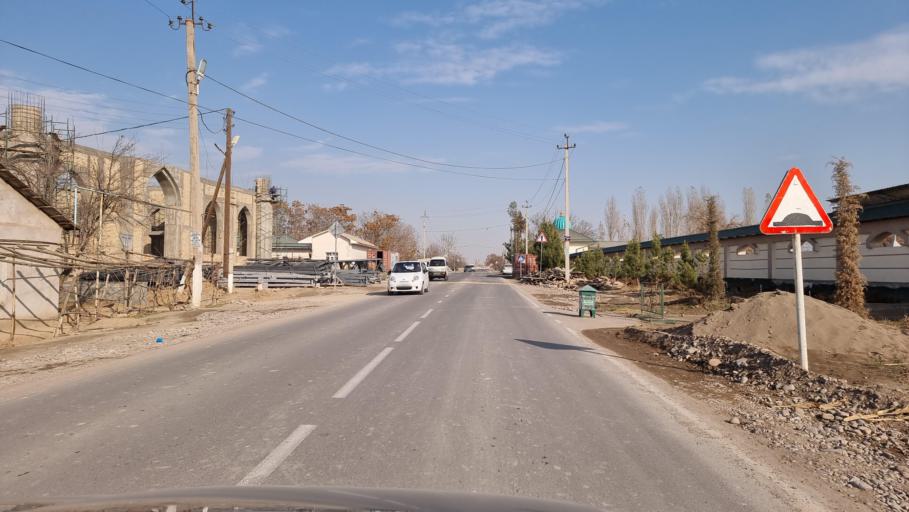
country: UZ
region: Toshkent
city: Urtaowul
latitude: 41.1875
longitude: 69.1199
